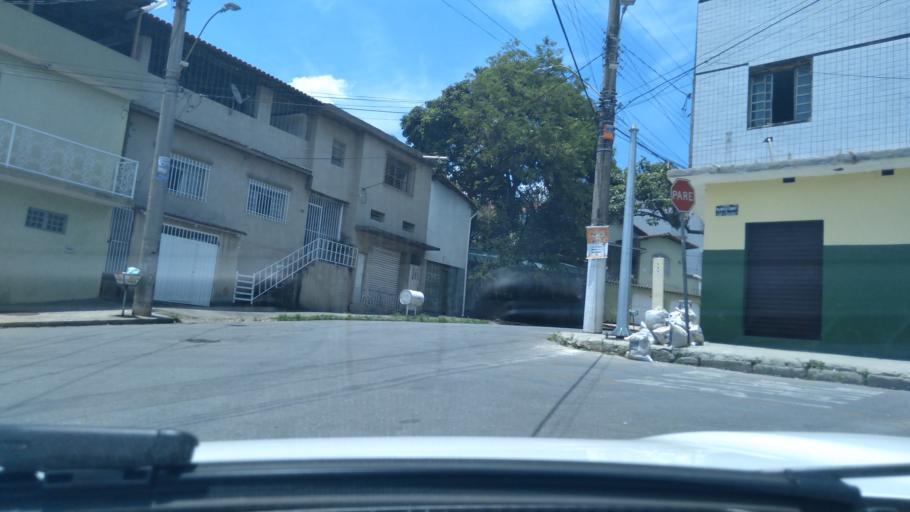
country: BR
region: Minas Gerais
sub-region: Contagem
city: Contagem
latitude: -19.9283
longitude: -44.0115
